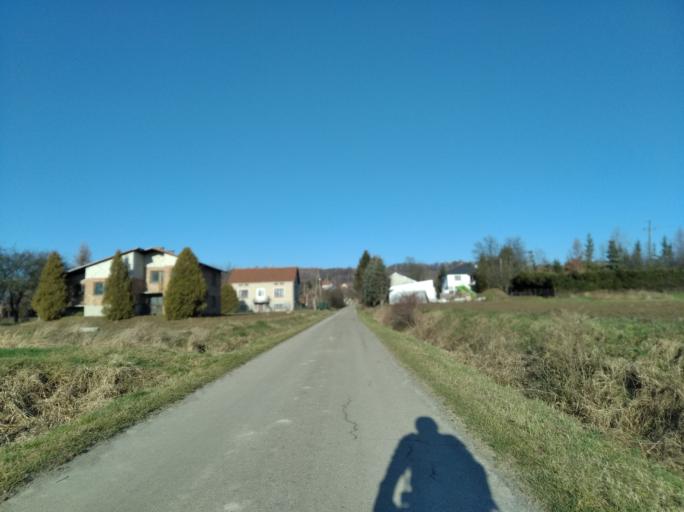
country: PL
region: Subcarpathian Voivodeship
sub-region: Powiat strzyzowski
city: Wisniowa
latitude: 49.8726
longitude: 21.6952
